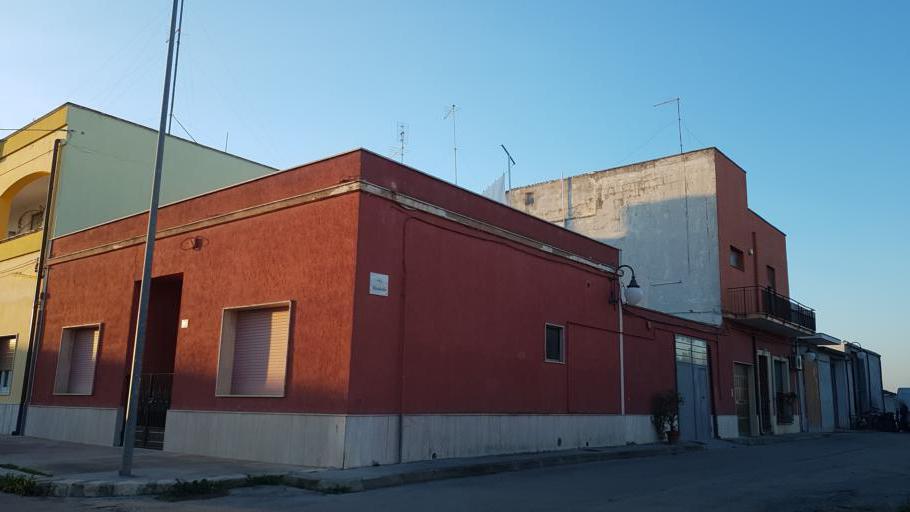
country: IT
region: Apulia
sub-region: Provincia di Brindisi
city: Tuturano
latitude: 40.5448
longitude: 17.9439
